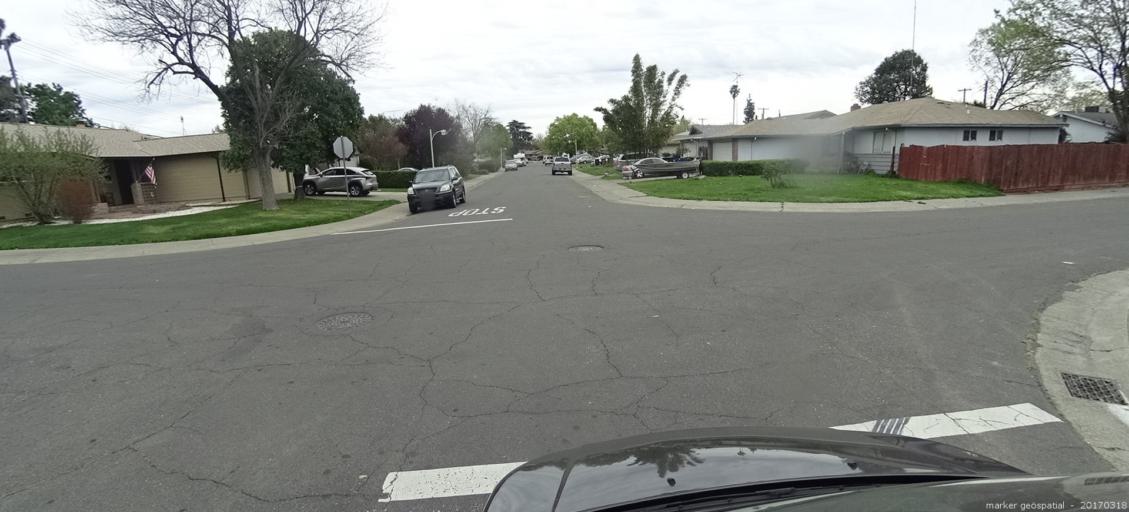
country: US
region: California
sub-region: Sacramento County
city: Parkway
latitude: 38.4848
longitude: -121.4509
